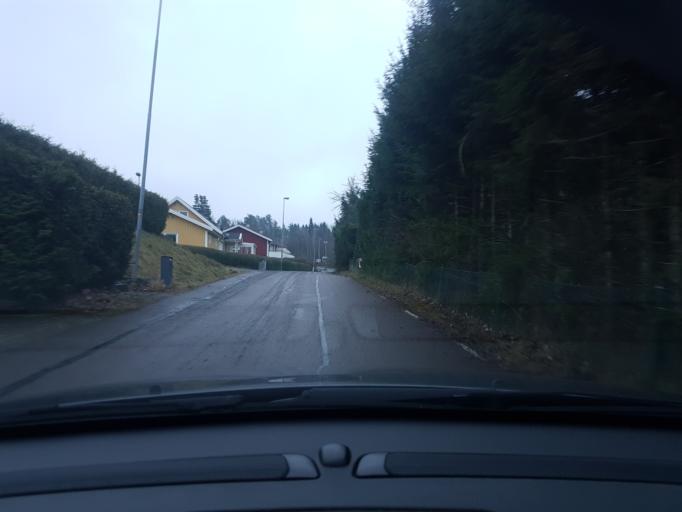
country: SE
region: Vaestra Goetaland
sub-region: Ale Kommun
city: Alvangen
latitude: 57.9507
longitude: 12.1318
